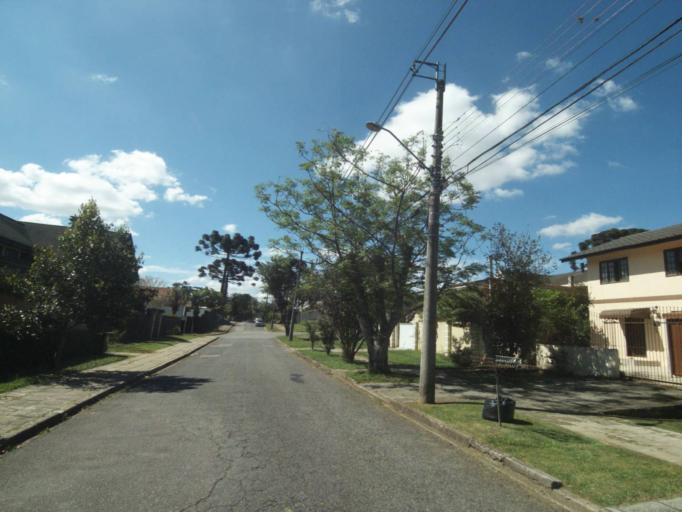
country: BR
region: Parana
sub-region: Curitiba
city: Curitiba
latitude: -25.4003
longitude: -49.2661
